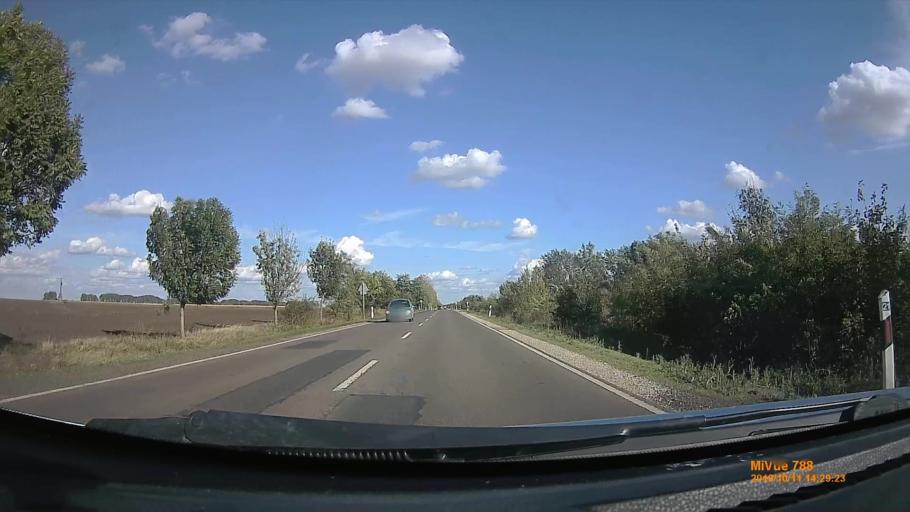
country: HU
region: Hajdu-Bihar
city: Balmazujvaros
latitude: 47.5584
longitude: 21.3815
